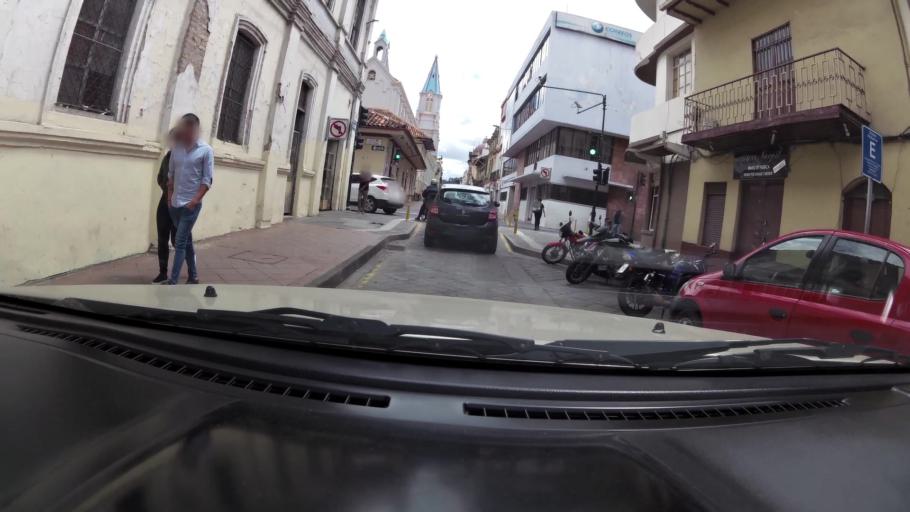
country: EC
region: Azuay
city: Cuenca
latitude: -2.8961
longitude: -79.0028
